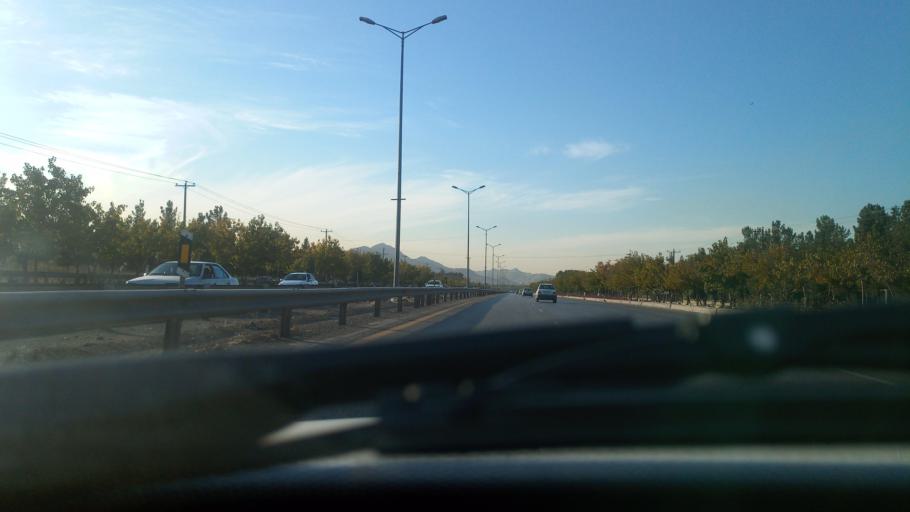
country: IR
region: Razavi Khorasan
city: Mashhad
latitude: 36.2073
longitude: 59.6410
